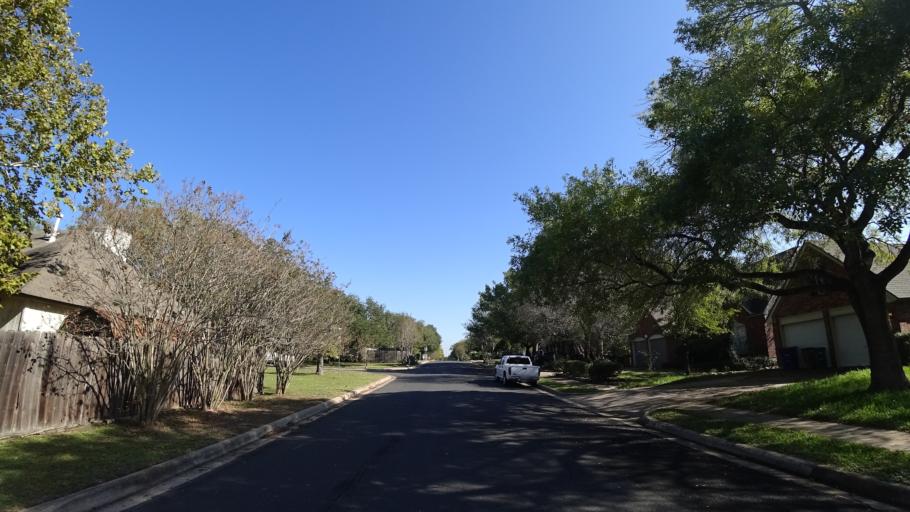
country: US
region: Texas
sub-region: Travis County
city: Shady Hollow
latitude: 30.1995
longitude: -97.8525
